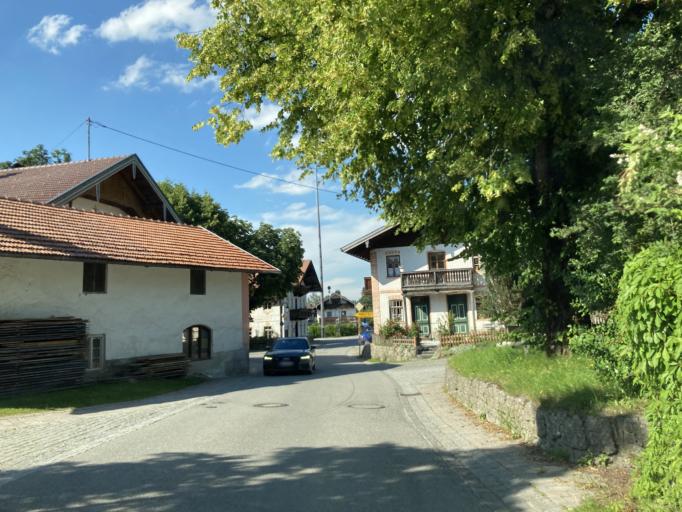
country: DE
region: Bavaria
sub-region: Upper Bavaria
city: Samerberg
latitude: 47.7752
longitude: 12.2350
